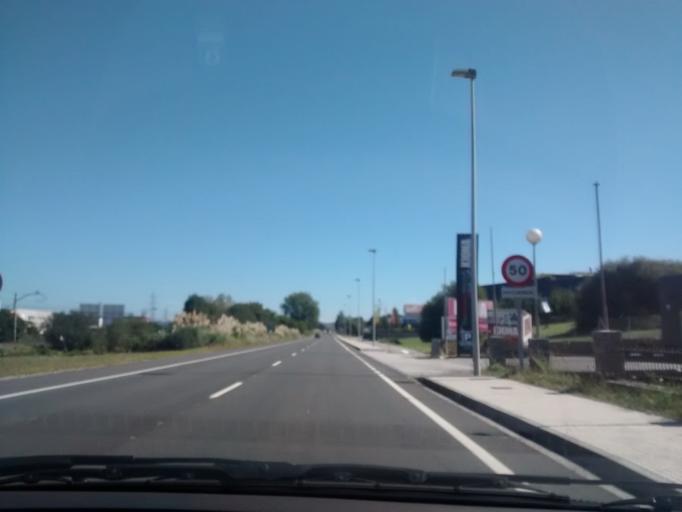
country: ES
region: Cantabria
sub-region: Provincia de Cantabria
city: El Astillero
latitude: 43.3951
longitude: -3.7946
